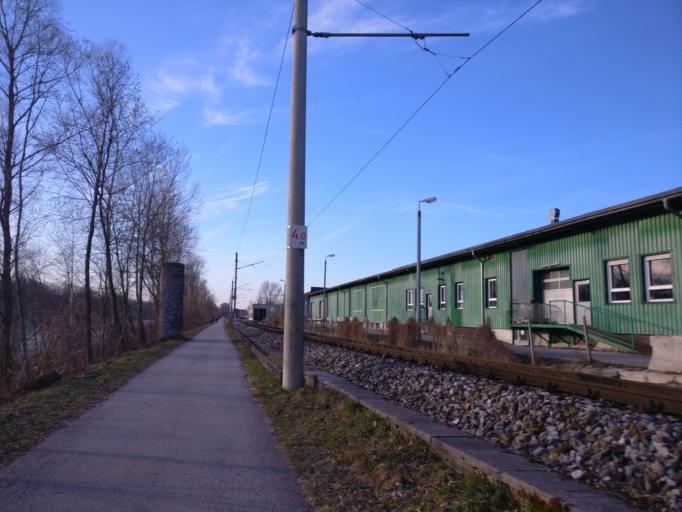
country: AT
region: Salzburg
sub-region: Politischer Bezirk Salzburg-Umgebung
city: Bergheim
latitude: 47.8422
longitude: 13.0169
